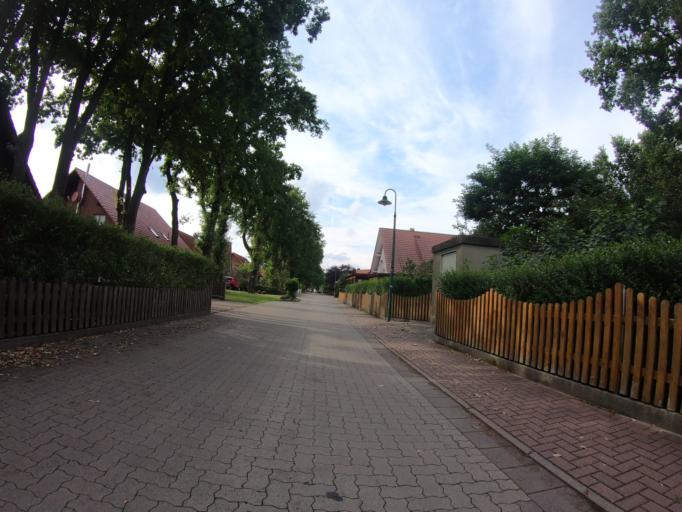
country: DE
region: Lower Saxony
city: Gifhorn
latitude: 52.5050
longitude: 10.5864
